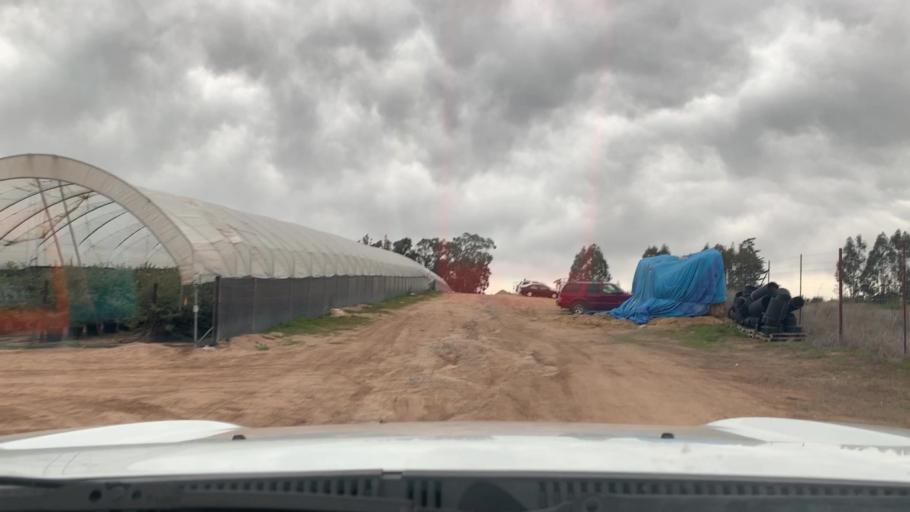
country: US
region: California
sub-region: San Luis Obispo County
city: Callender
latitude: 35.0646
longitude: -120.5674
